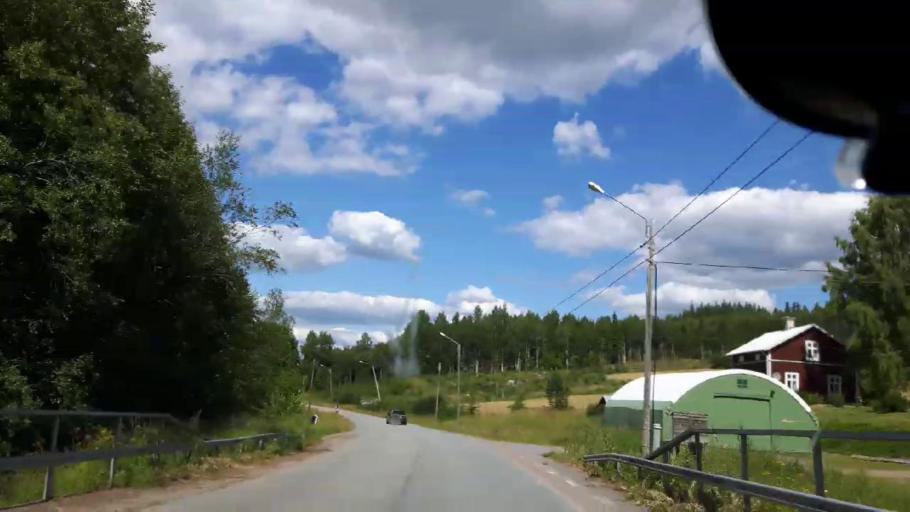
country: SE
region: Jaemtland
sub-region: Ragunda Kommun
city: Hammarstrand
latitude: 62.9423
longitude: 16.6921
